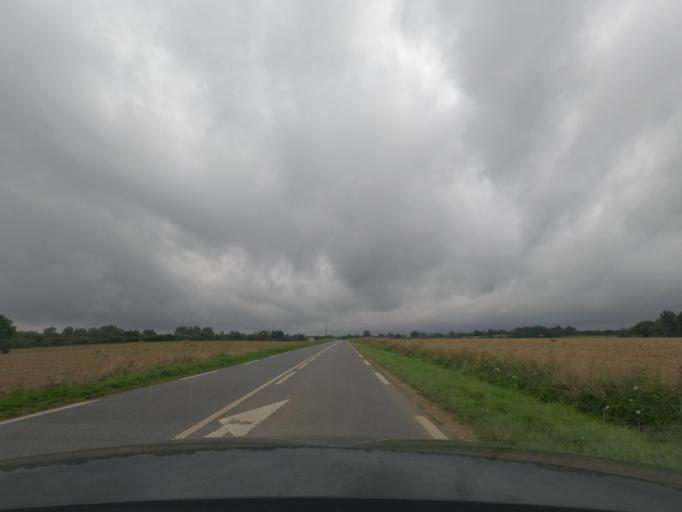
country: FR
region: Haute-Normandie
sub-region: Departement de la Seine-Maritime
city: Forges-les-Eaux
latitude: 49.6279
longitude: 1.5749
